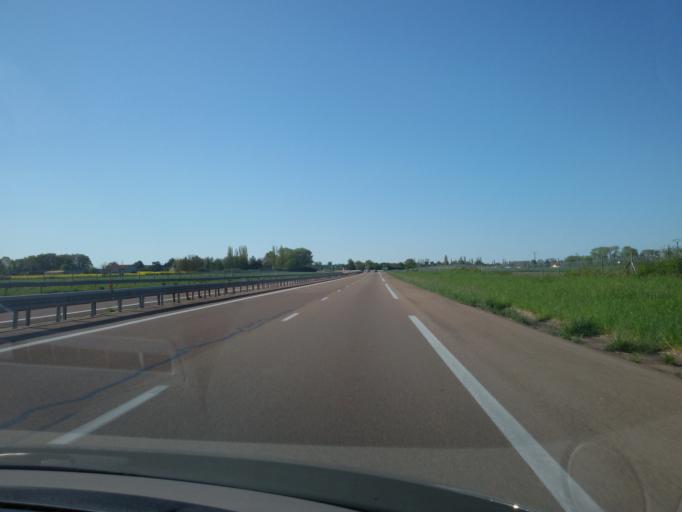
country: FR
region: Bourgogne
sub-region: Departement de l'Yonne
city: Venoy
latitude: 47.8240
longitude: 3.6237
